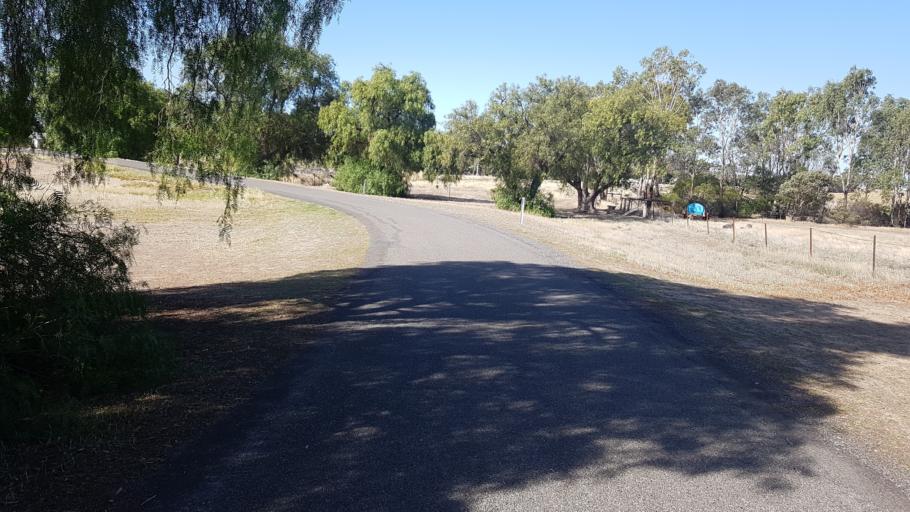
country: AU
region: Victoria
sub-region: Horsham
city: Horsham
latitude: -36.7444
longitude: 141.9426
